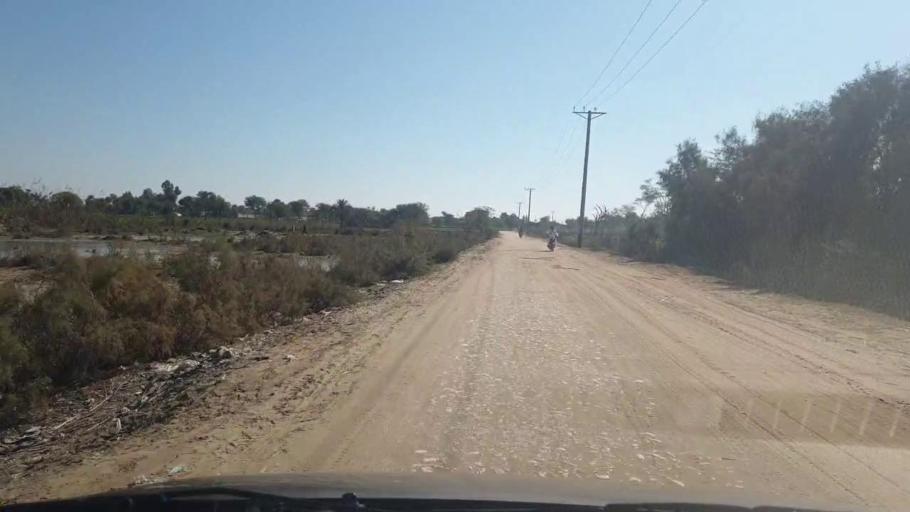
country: PK
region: Sindh
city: Bozdar
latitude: 27.0738
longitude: 68.6165
